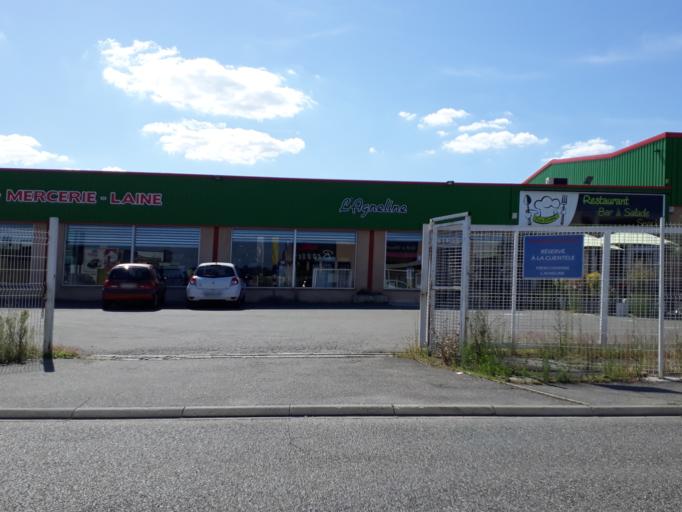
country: FR
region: Midi-Pyrenees
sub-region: Departement de la Haute-Garonne
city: Beauzelle
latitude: 43.6677
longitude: 1.3643
